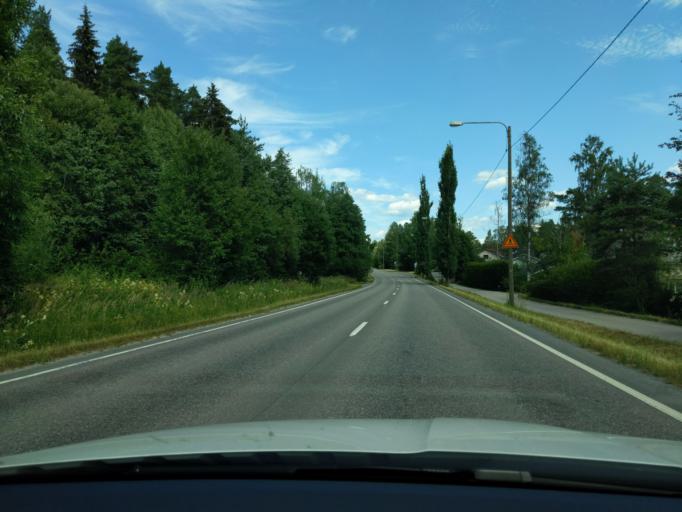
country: FI
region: Paijanne Tavastia
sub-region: Lahti
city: Lahti
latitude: 61.0179
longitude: 25.7175
